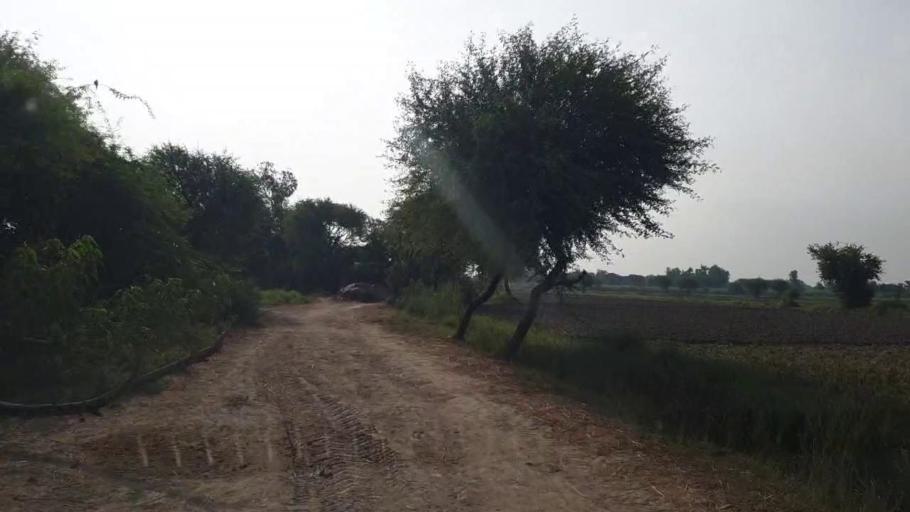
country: PK
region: Sindh
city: Rajo Khanani
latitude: 24.9081
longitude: 68.9202
